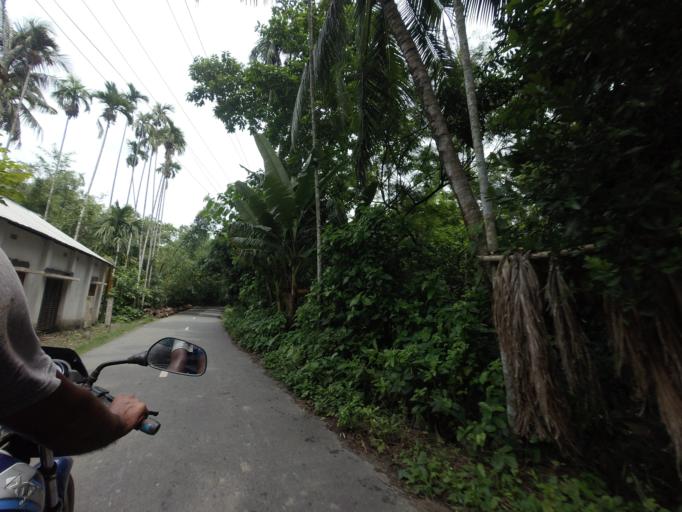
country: BD
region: Khulna
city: Kalia
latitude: 23.0868
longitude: 89.6645
